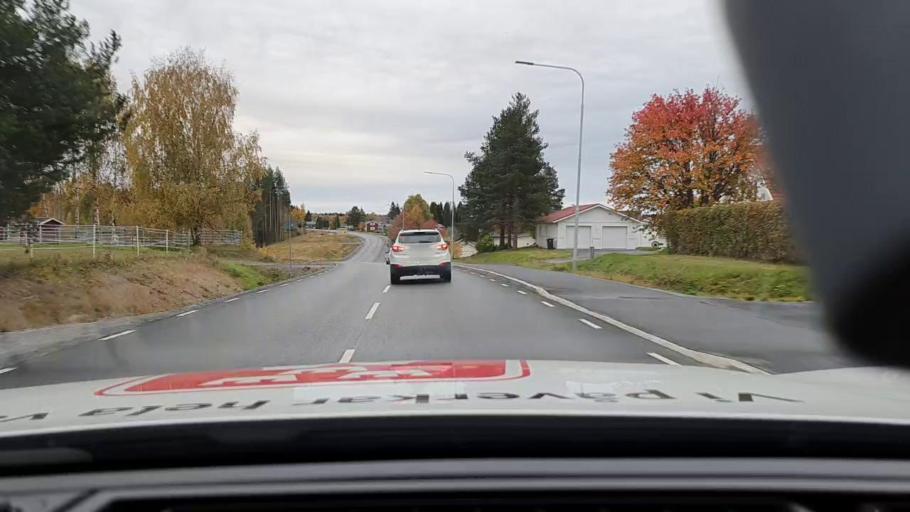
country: SE
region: Norrbotten
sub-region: Bodens Kommun
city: Saevast
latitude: 65.7772
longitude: 21.6930
